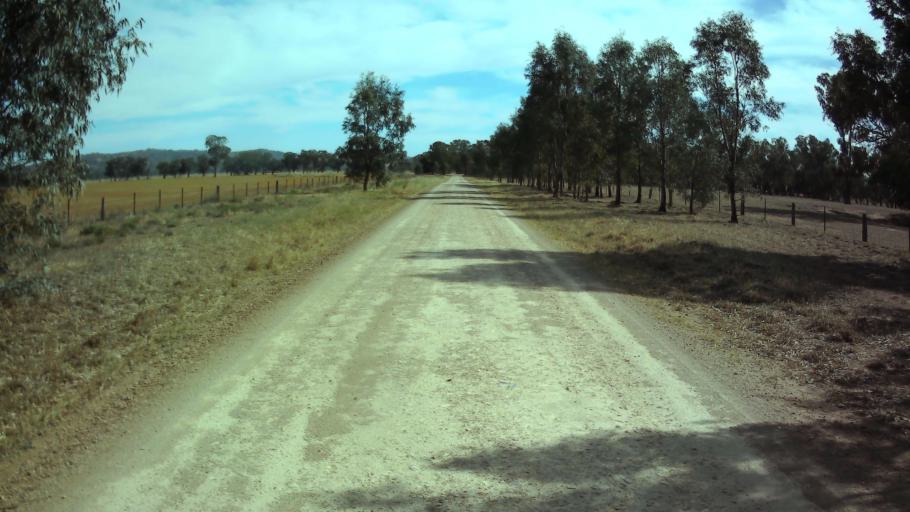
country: AU
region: New South Wales
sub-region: Weddin
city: Grenfell
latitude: -33.7062
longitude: 148.3012
